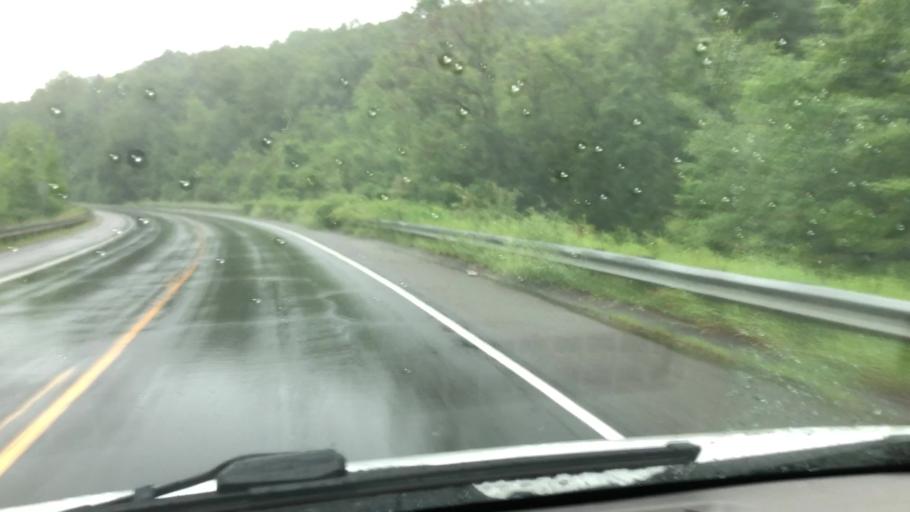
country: US
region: Massachusetts
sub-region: Berkshire County
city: Pittsfield
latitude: 42.4161
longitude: -73.2747
